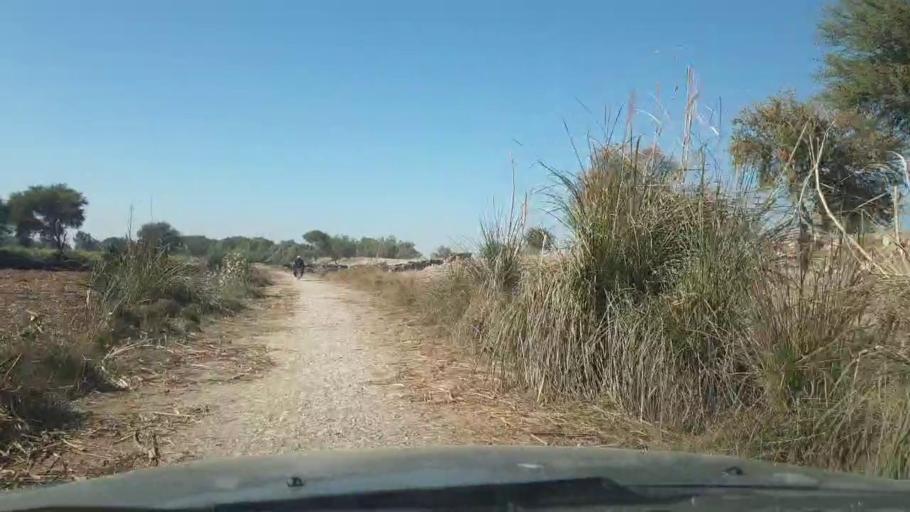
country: PK
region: Sindh
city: Ghotki
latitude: 28.0575
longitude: 69.2403
